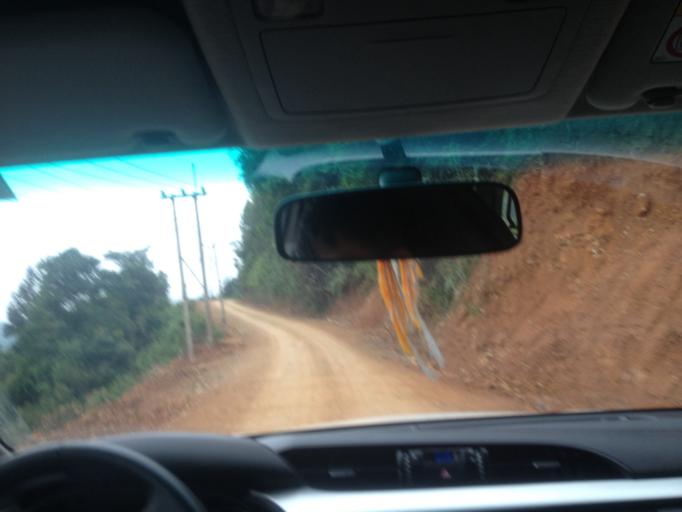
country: TH
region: Nan
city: Chaloem Phra Kiat
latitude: 19.9923
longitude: 101.1385
